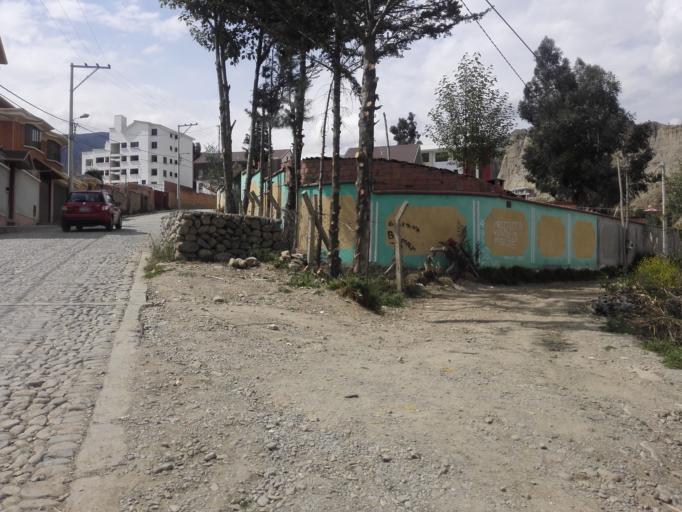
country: BO
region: La Paz
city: La Paz
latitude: -16.5043
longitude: -68.0814
